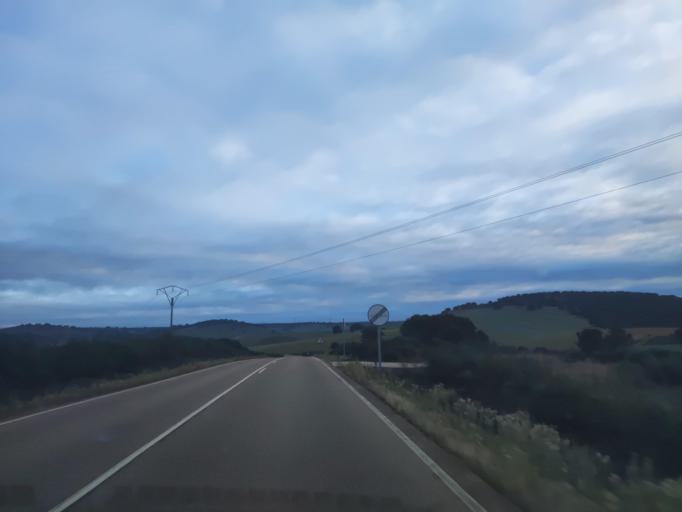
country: ES
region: Castille and Leon
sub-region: Provincia de Salamanca
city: Castillejo de Martin Viejo
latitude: 40.7201
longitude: -6.6404
